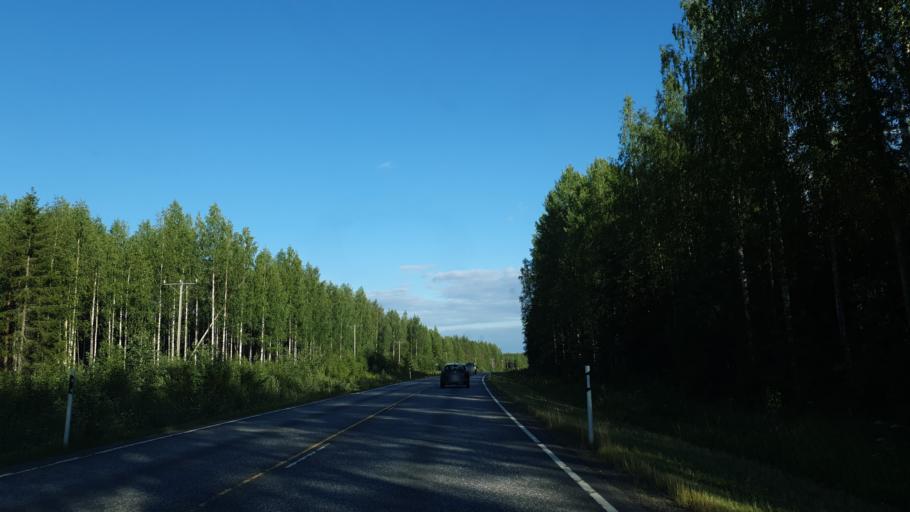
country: FI
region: North Karelia
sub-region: Joensuu
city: Outokumpu
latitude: 62.5300
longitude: 28.9843
